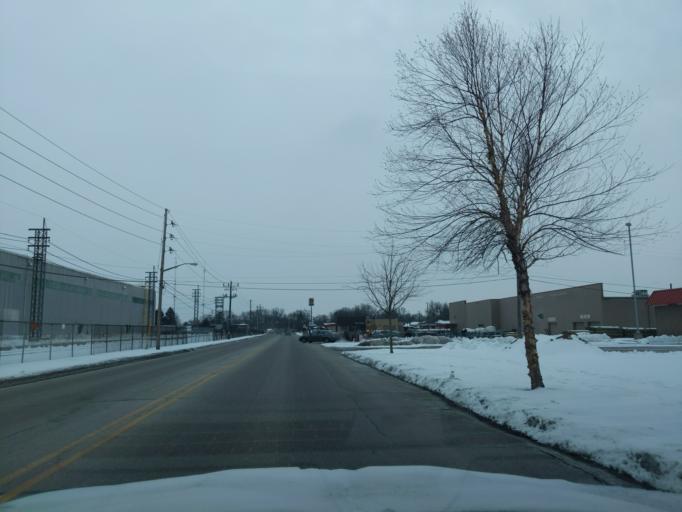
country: US
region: Indiana
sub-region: Tippecanoe County
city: Lafayette
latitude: 40.3988
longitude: -86.8671
